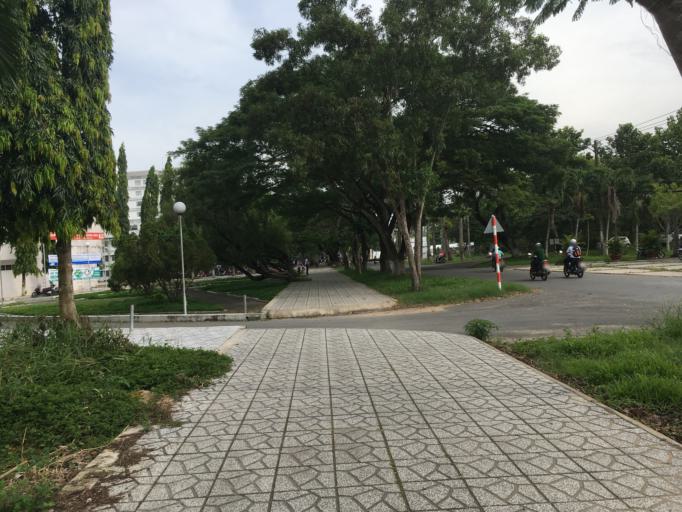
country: VN
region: Can Tho
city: Can Tho
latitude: 10.0308
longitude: 105.7684
